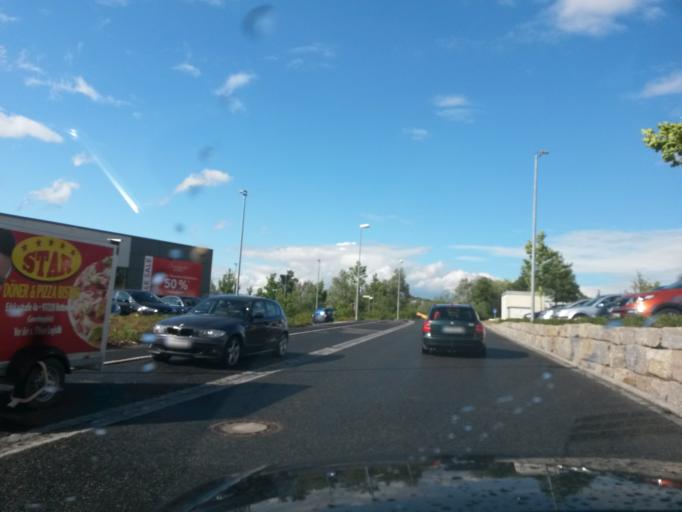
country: DE
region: Bavaria
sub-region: Regierungsbezirk Unterfranken
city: Rottendorf
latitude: 49.7869
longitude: 10.0307
